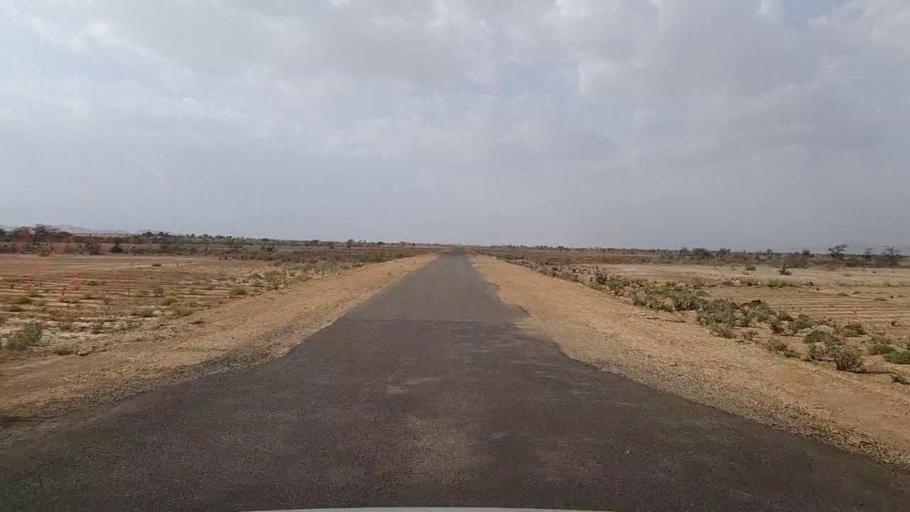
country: PK
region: Sindh
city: Jamshoro
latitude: 25.4527
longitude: 67.6779
